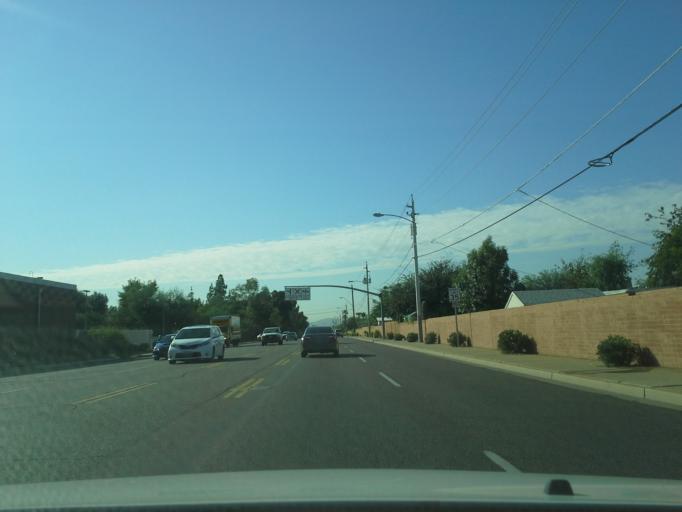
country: US
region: Arizona
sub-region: Maricopa County
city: Phoenix
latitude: 33.4936
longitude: -112.0835
